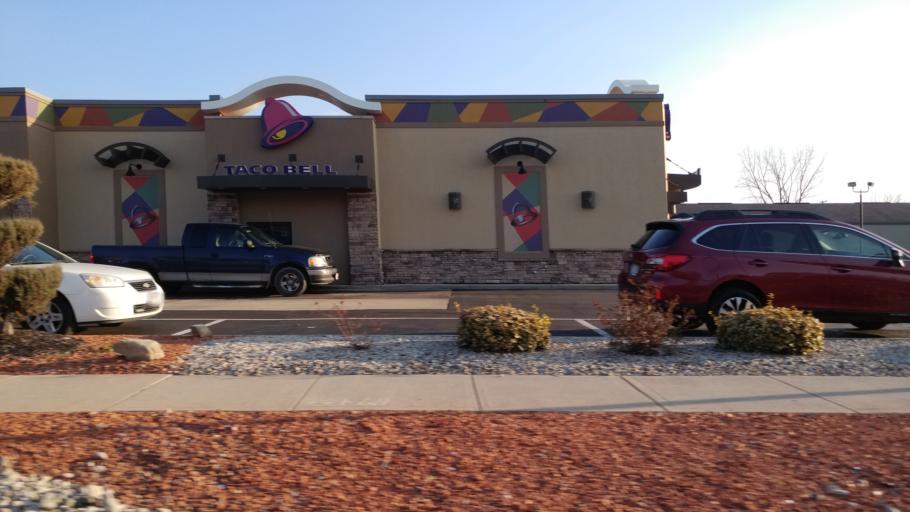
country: US
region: Ohio
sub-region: Hancock County
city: Findlay
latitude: 41.0491
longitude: -83.6292
